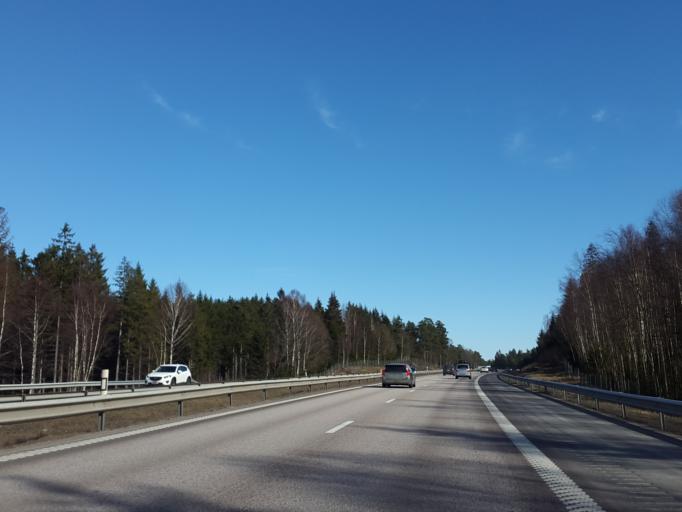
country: SE
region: Vaestra Goetaland
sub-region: Harryda Kommun
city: Landvetter
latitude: 57.7420
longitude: 12.1980
